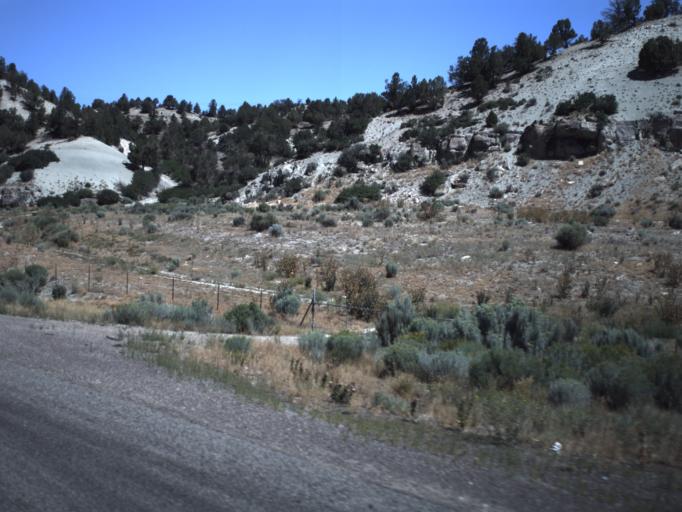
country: US
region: Utah
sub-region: Utah County
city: Mapleton
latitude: 39.9623
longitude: -111.3055
